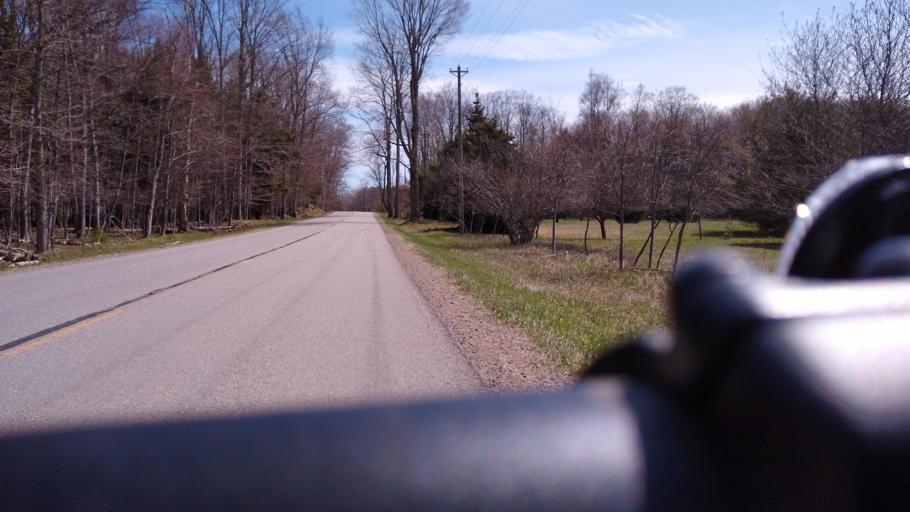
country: US
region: Michigan
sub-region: Delta County
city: Escanaba
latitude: 45.6982
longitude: -87.1629
